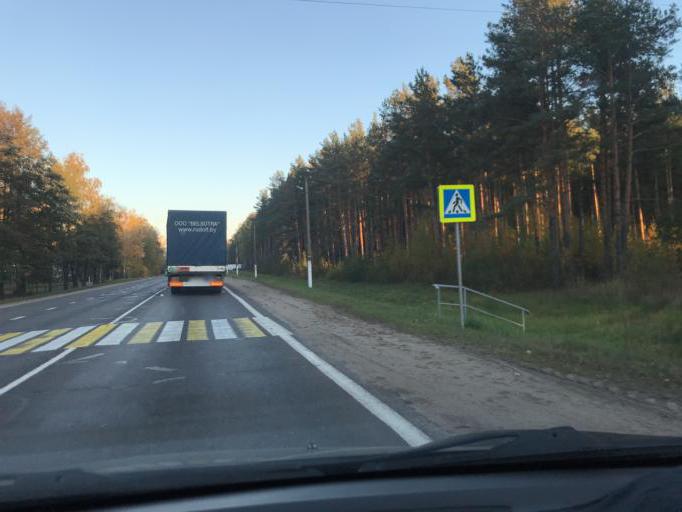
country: BY
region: Minsk
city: Staryya Darohi
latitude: 53.0337
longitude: 28.2457
